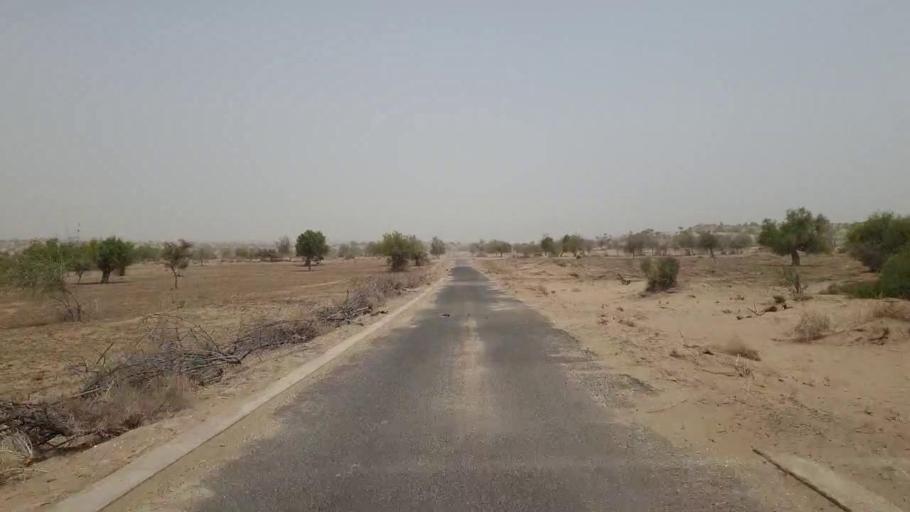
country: PK
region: Sindh
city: Islamkot
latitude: 24.8098
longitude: 70.5346
